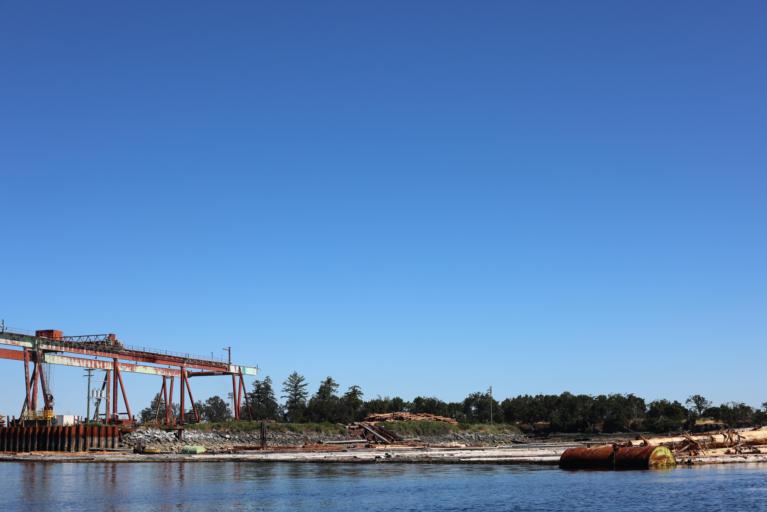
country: CA
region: British Columbia
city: North Cowichan
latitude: 48.8780
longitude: -123.6339
